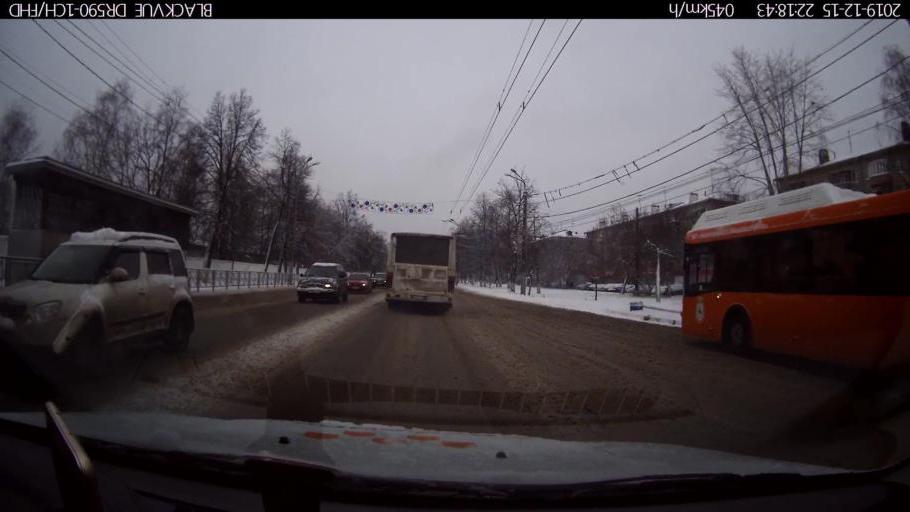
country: RU
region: Nizjnij Novgorod
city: Nizhniy Novgorod
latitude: 56.3231
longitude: 43.9190
